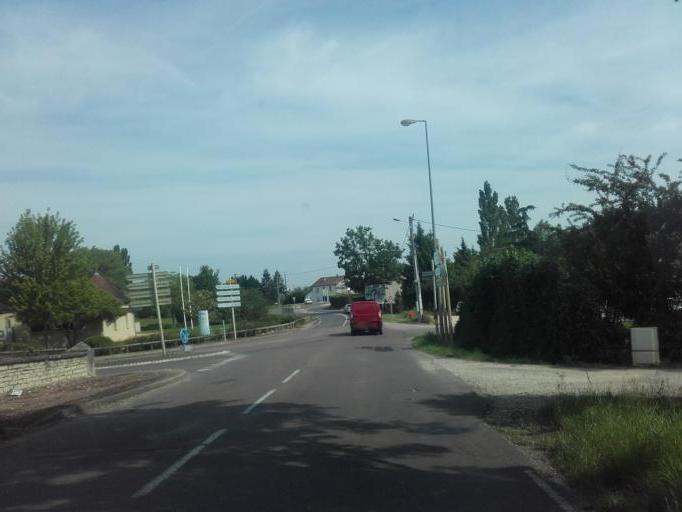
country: FR
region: Bourgogne
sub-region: Departement de Saone-et-Loire
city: Dracy-le-Fort
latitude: 46.8144
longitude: 4.7524
